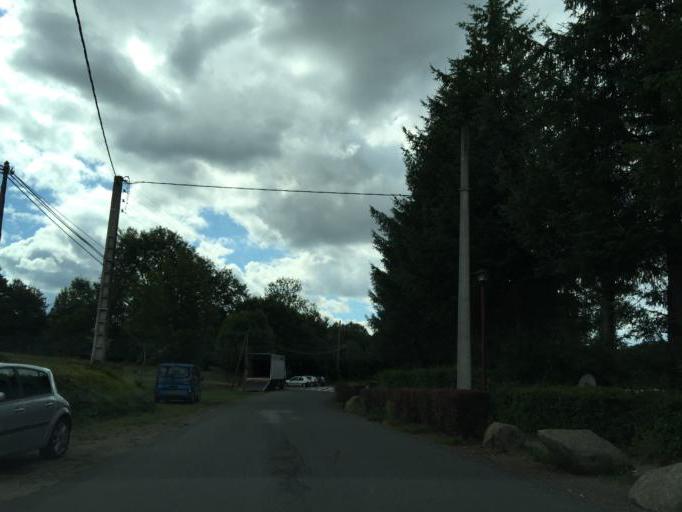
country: FR
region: Midi-Pyrenees
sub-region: Departement de l'Aveyron
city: Pont-de-Salars
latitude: 44.2914
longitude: 2.7252
